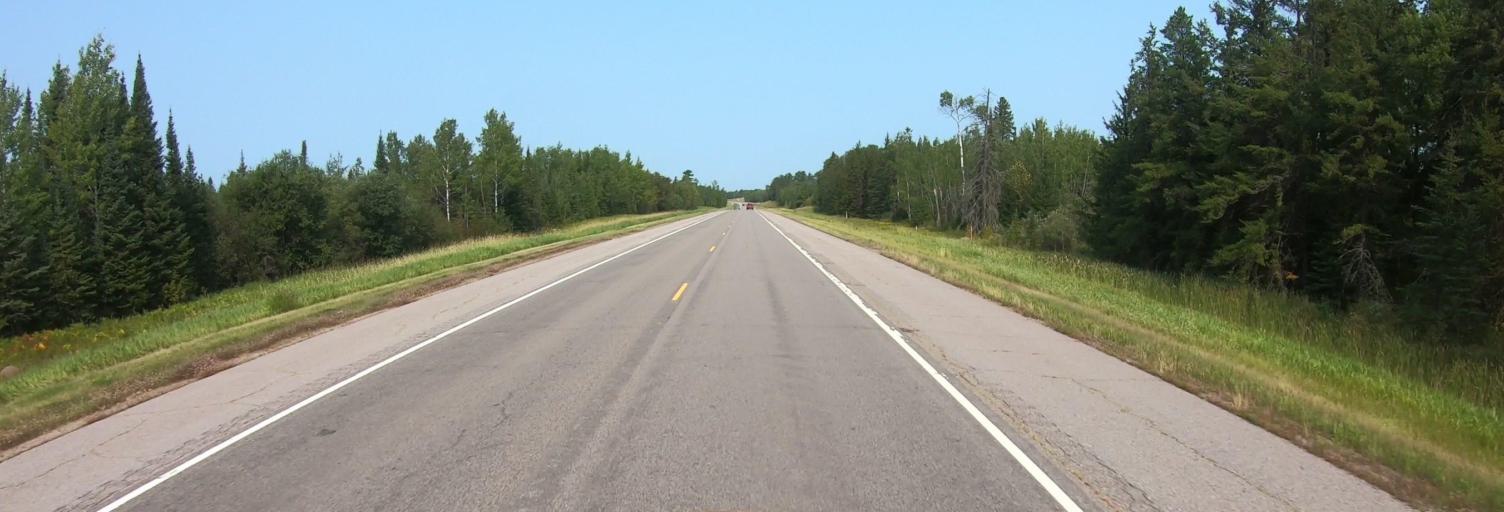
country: US
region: Minnesota
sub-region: Saint Louis County
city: Mountain Iron
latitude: 47.8805
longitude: -92.7628
